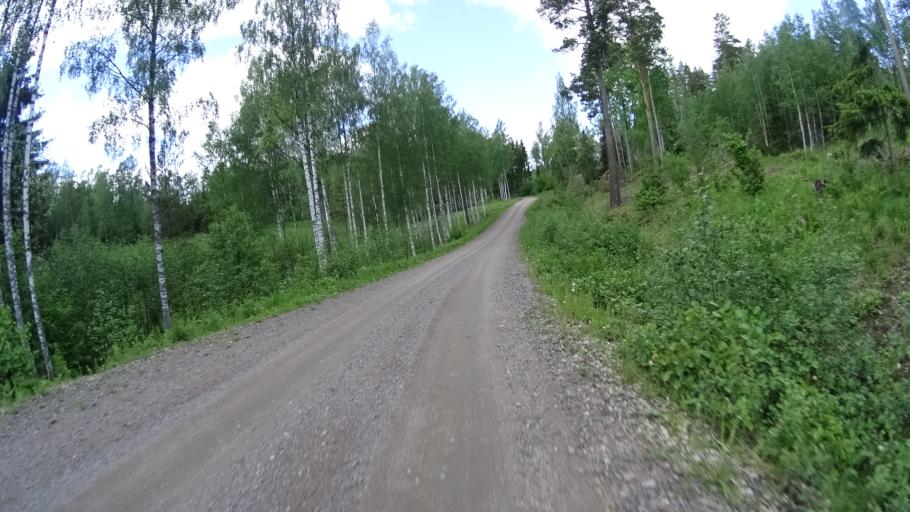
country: FI
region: Uusimaa
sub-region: Raaseporin
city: Karis
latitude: 60.1404
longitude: 23.6221
